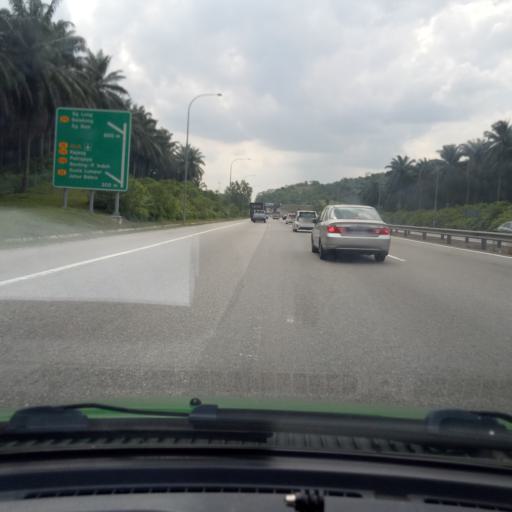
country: MY
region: Selangor
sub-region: Hulu Langat
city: Semenyih
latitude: 2.9819
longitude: 101.8333
